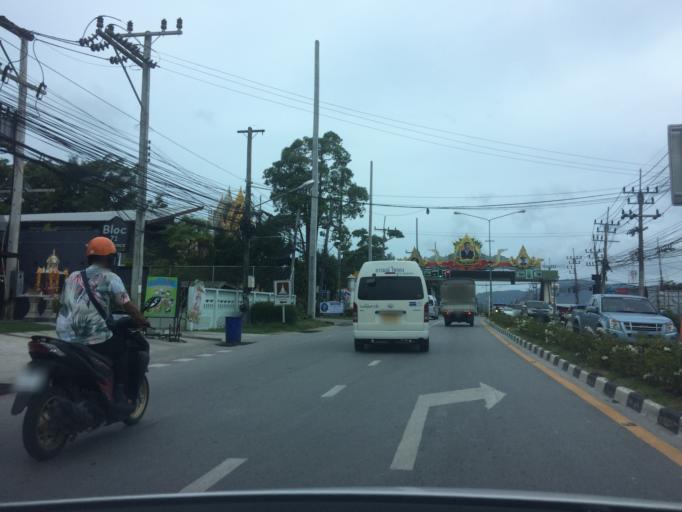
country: TH
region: Phuket
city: Mueang Phuket
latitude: 7.8615
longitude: 98.3690
